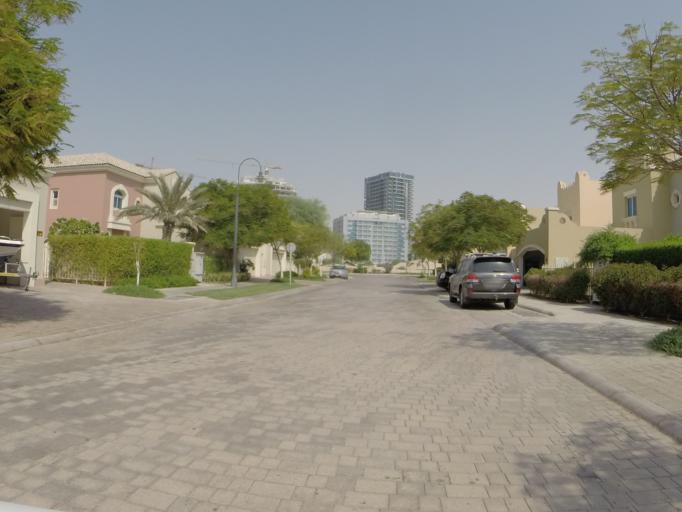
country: AE
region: Dubai
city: Dubai
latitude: 25.0344
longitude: 55.2185
